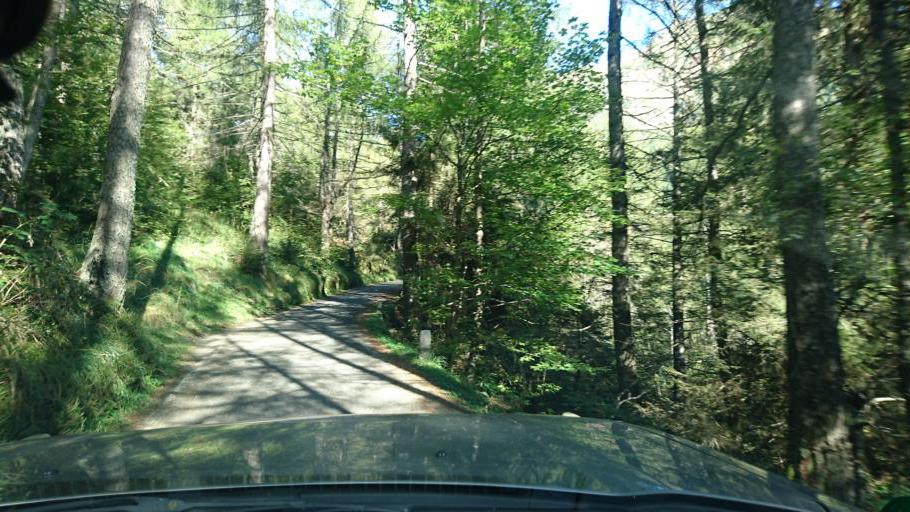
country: IT
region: Lombardy
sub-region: Provincia di Brescia
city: Lozio
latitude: 46.0483
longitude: 10.2226
